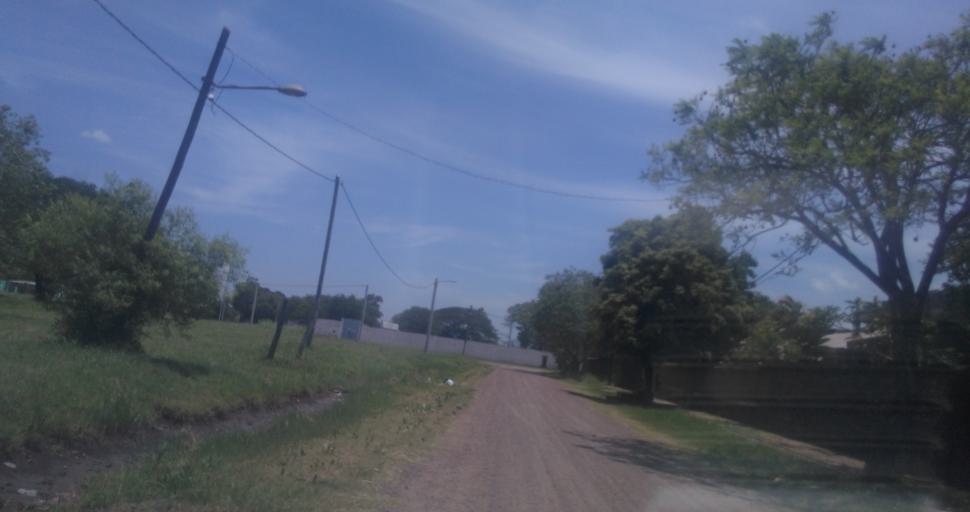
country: AR
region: Chaco
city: Fontana
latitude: -27.4172
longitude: -59.0346
